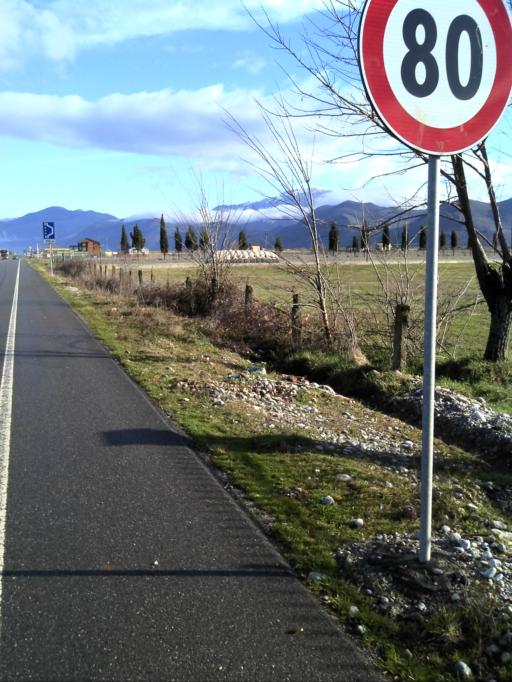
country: AL
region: Shkoder
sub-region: Rrethi i Malesia e Madhe
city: Koplik
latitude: 42.2482
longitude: 19.4257
